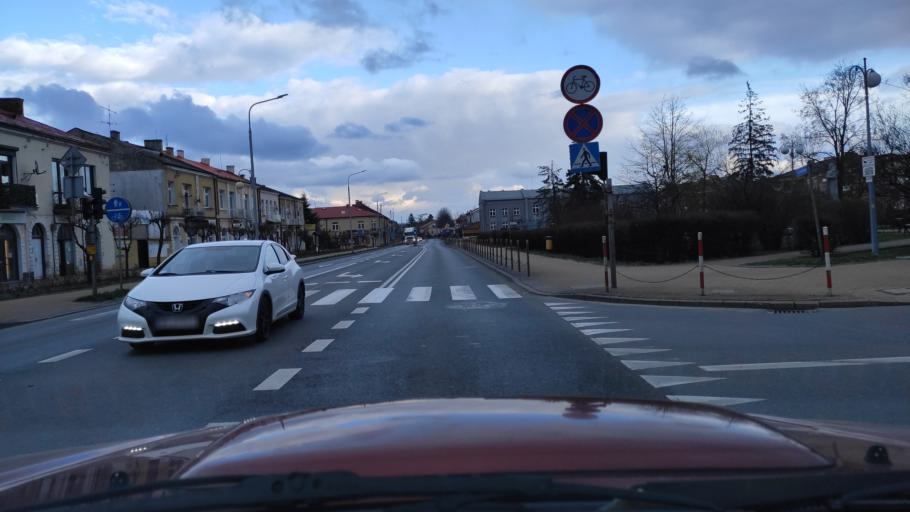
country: PL
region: Masovian Voivodeship
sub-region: Powiat zwolenski
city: Zwolen
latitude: 51.3569
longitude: 21.5837
